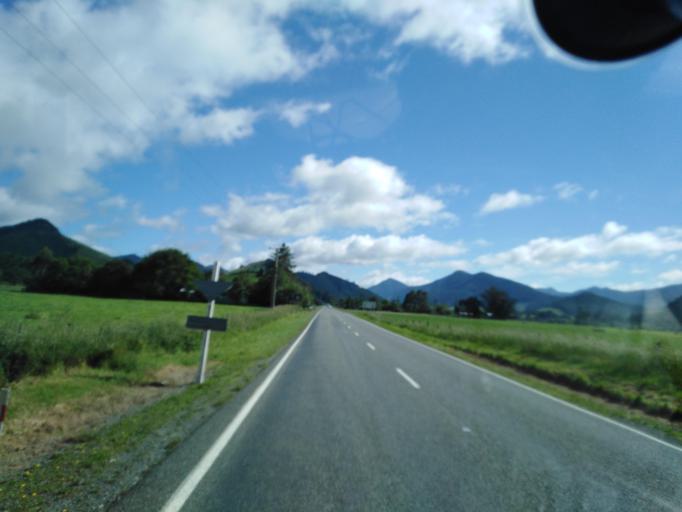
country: NZ
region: Nelson
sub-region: Nelson City
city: Nelson
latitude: -41.2417
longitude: 173.5785
